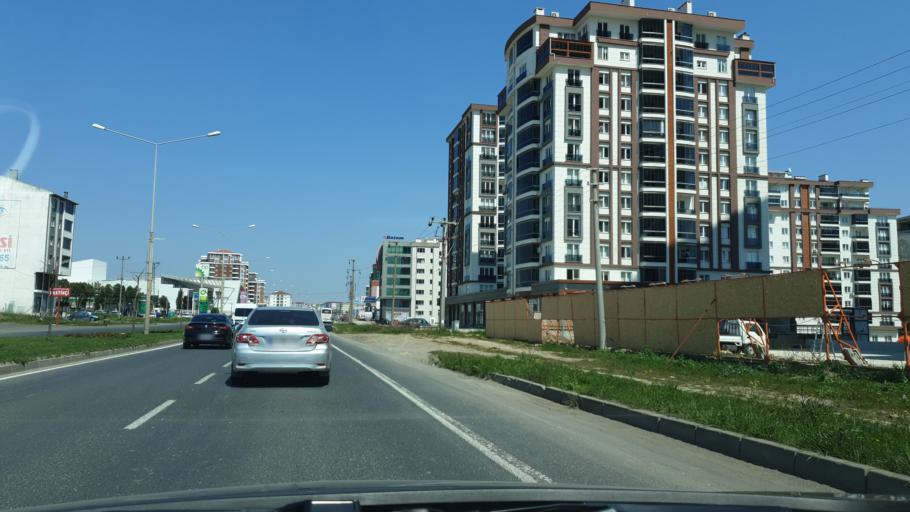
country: TR
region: Tekirdag
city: Corlu
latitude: 41.1514
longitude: 27.7781
